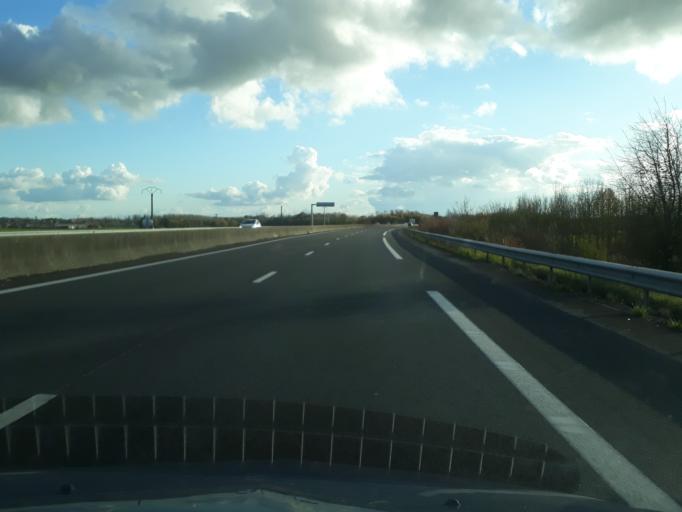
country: FR
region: Champagne-Ardenne
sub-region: Departement de la Marne
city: Fagnieres
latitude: 49.0056
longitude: 4.2987
